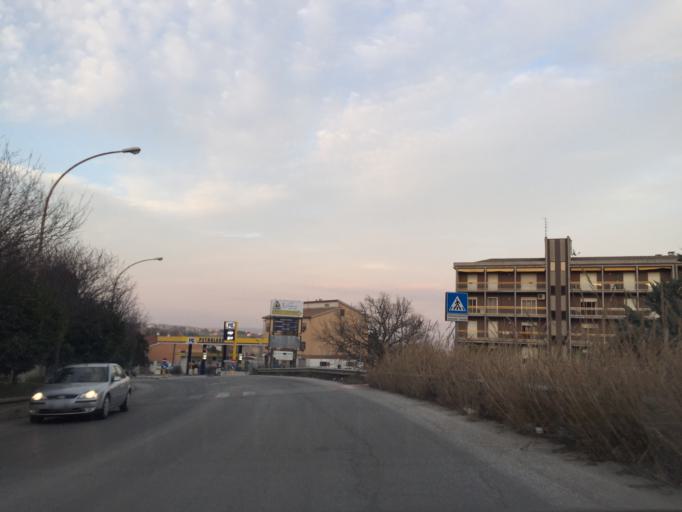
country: IT
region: Molise
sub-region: Provincia di Campobasso
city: Campobasso
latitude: 41.5604
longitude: 14.6818
